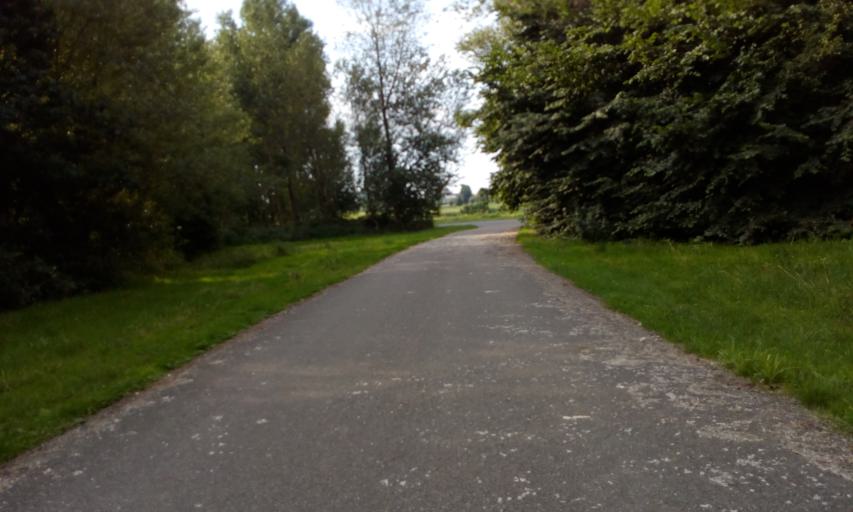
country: NL
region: South Holland
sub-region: Gemeente Lansingerland
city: Bleiswijk
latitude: 51.9742
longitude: 4.5398
